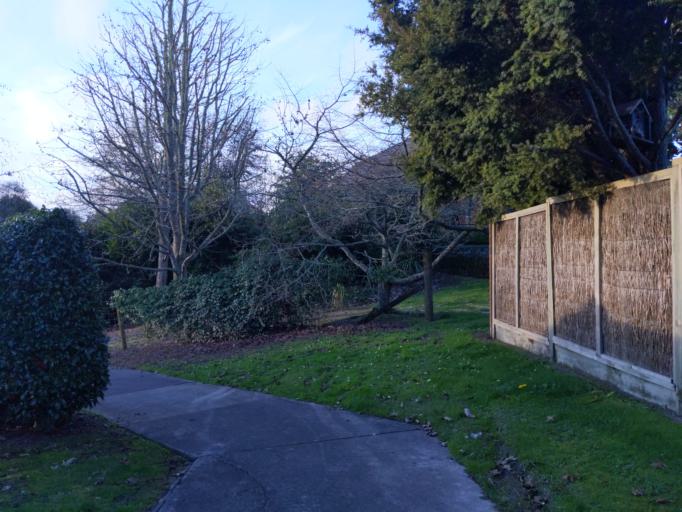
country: NZ
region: Waikato
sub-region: Hamilton City
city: Hamilton
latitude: -37.7417
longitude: 175.2766
